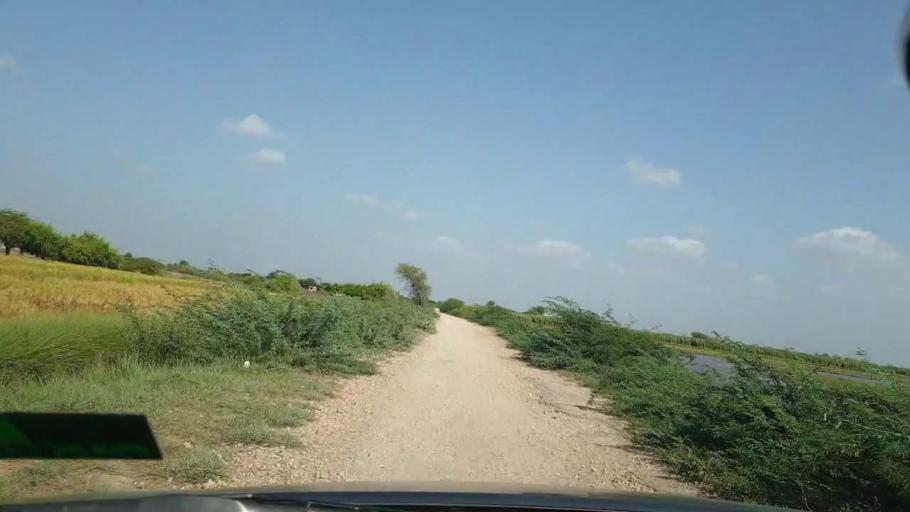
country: PK
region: Sindh
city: Tando Bago
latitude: 24.6828
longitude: 69.1897
